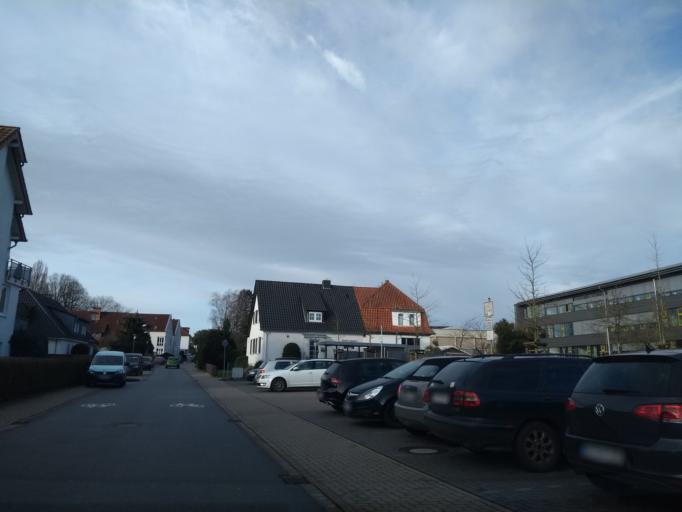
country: DE
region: North Rhine-Westphalia
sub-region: Regierungsbezirk Detmold
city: Lemgo
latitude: 52.0317
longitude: 8.8970
